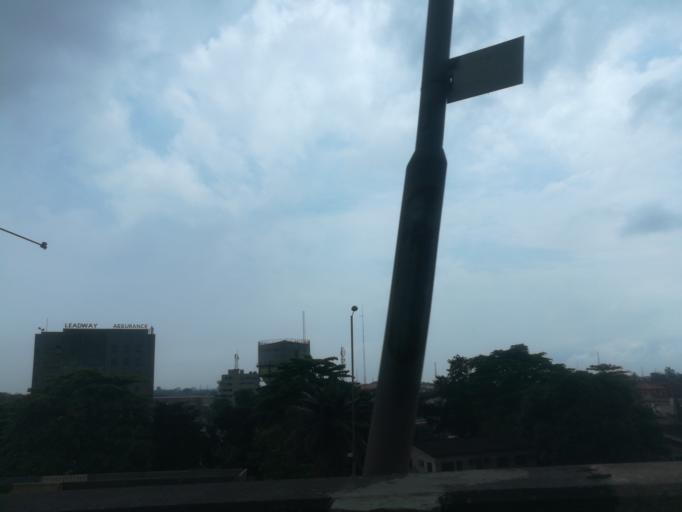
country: NG
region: Lagos
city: Surulere
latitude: 6.4844
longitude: 3.3654
